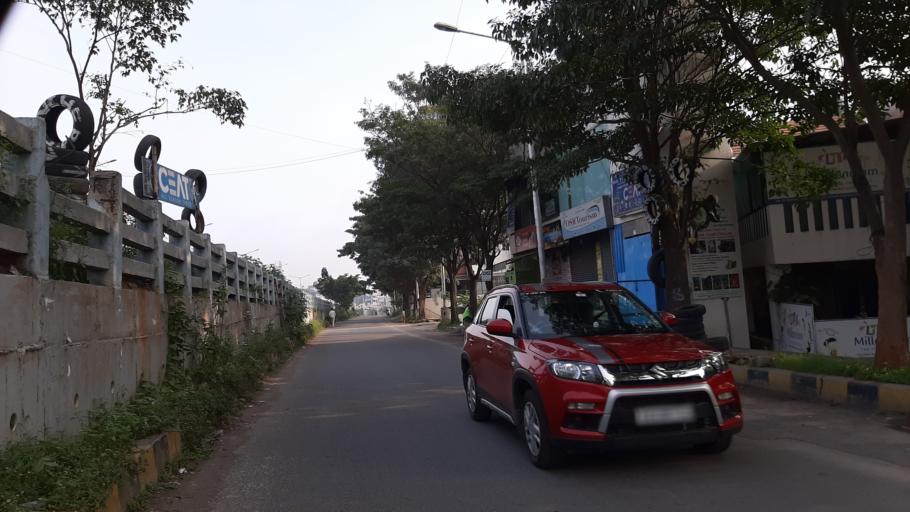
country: IN
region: Karnataka
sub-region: Bangalore Urban
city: Bangalore
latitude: 12.9717
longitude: 77.5129
